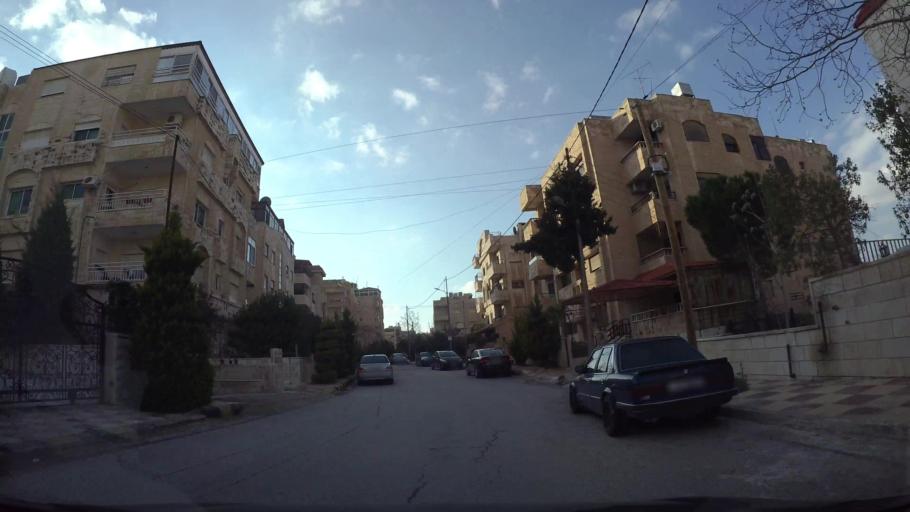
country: JO
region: Amman
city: Al Jubayhah
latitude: 31.9825
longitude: 35.8852
